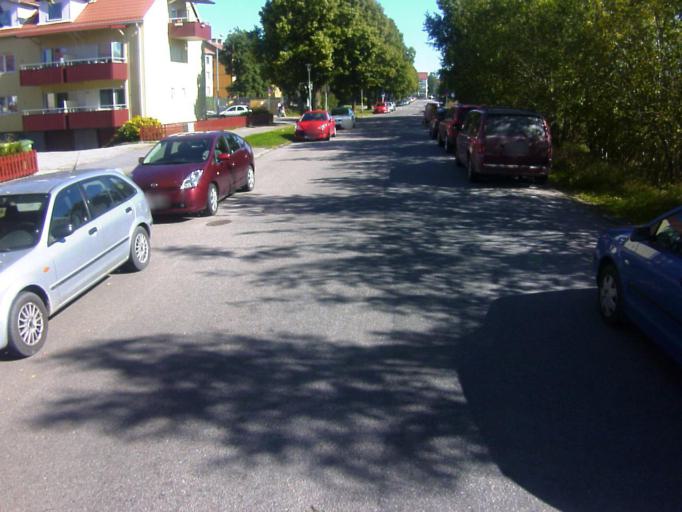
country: SE
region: Soedermanland
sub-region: Eskilstuna Kommun
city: Eskilstuna
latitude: 59.3799
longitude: 16.5164
